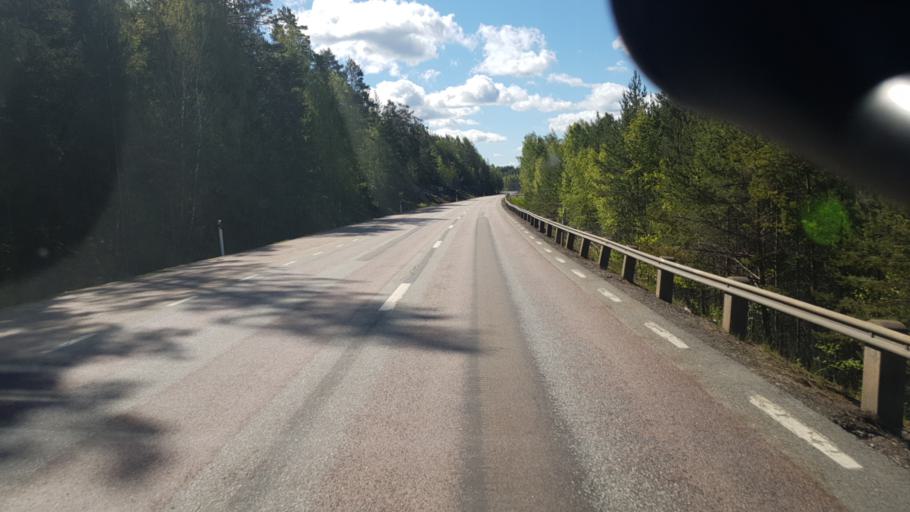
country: SE
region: Vaermland
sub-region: Arvika Kommun
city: Arvika
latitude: 59.5628
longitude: 12.7221
